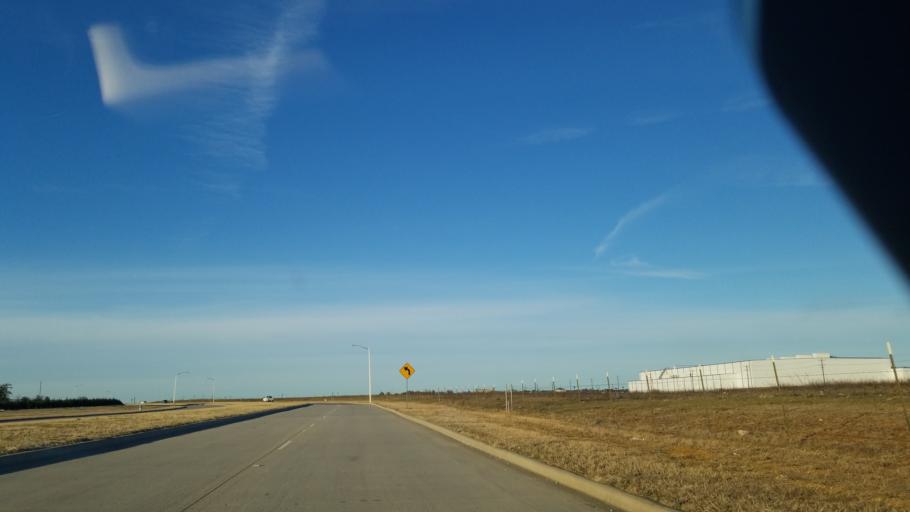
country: US
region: Texas
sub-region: Denton County
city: Denton
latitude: 33.2118
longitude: -97.1844
